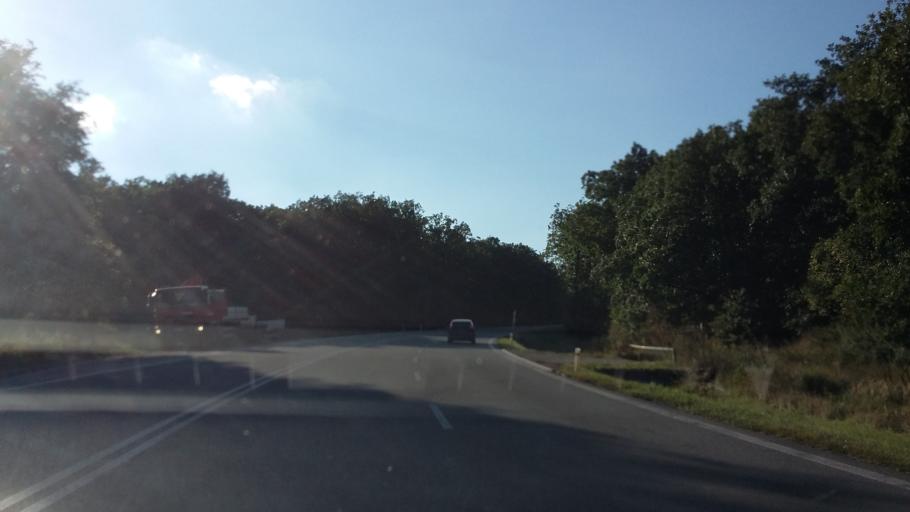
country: CZ
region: South Moravian
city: Troubsko
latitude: 49.1844
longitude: 16.4759
